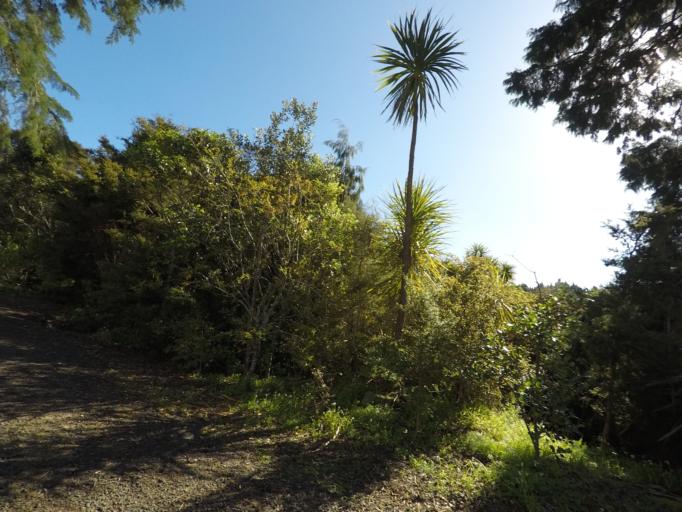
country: NZ
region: Auckland
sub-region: Auckland
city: Rosebank
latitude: -36.8614
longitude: 174.5950
